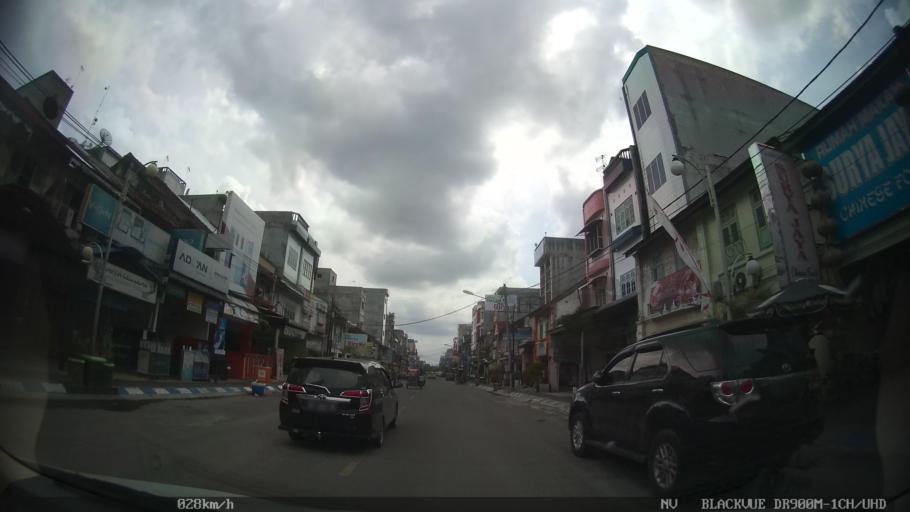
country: ID
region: North Sumatra
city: Percut
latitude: 3.5622
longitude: 98.8771
